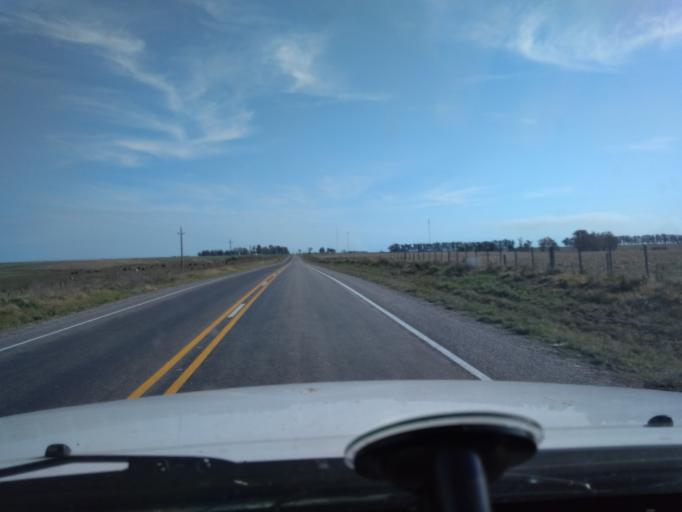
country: UY
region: Florida
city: Casupa
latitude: -34.0278
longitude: -55.8709
